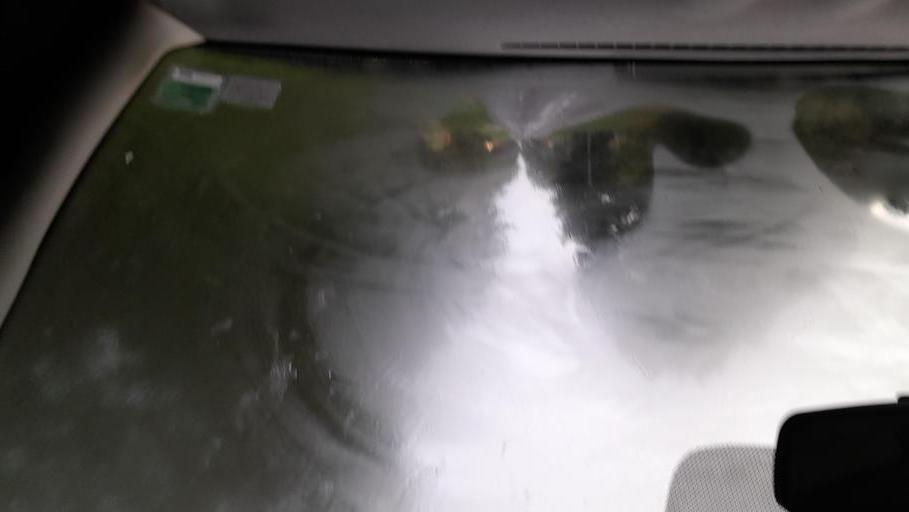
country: FR
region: Pays de la Loire
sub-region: Departement de la Mayenne
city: Ballots
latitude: 47.8753
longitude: -1.0465
